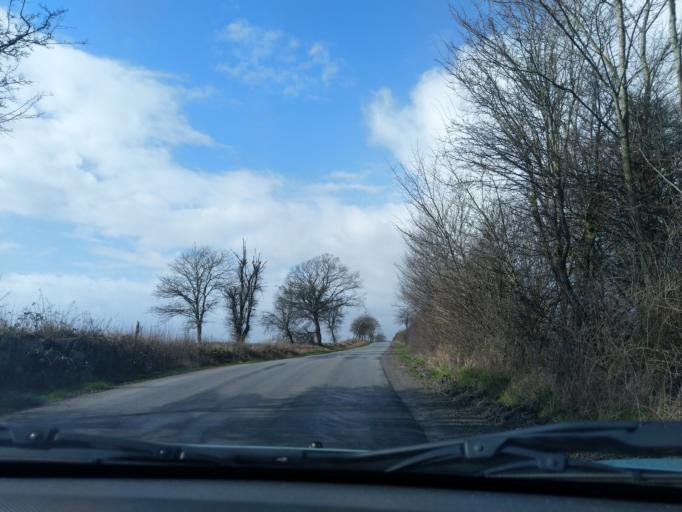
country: DK
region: Zealand
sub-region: Naestved Kommune
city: Fuglebjerg
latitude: 55.3145
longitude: 11.6650
